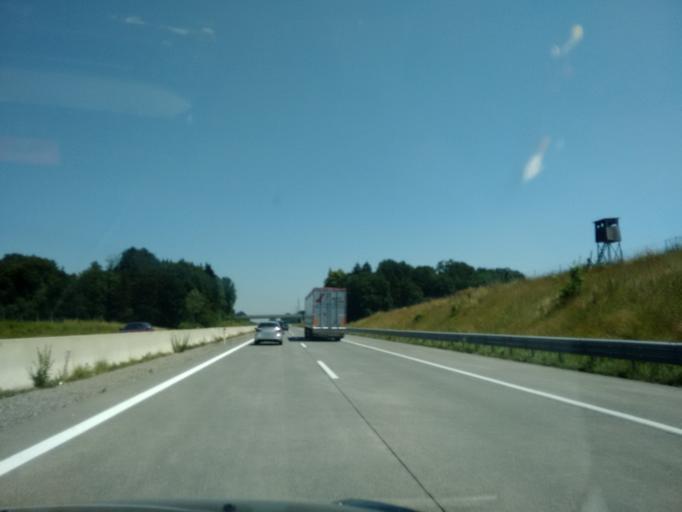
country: AT
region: Upper Austria
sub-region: Politischer Bezirk Gmunden
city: Vorchdorf
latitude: 48.0033
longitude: 13.8747
